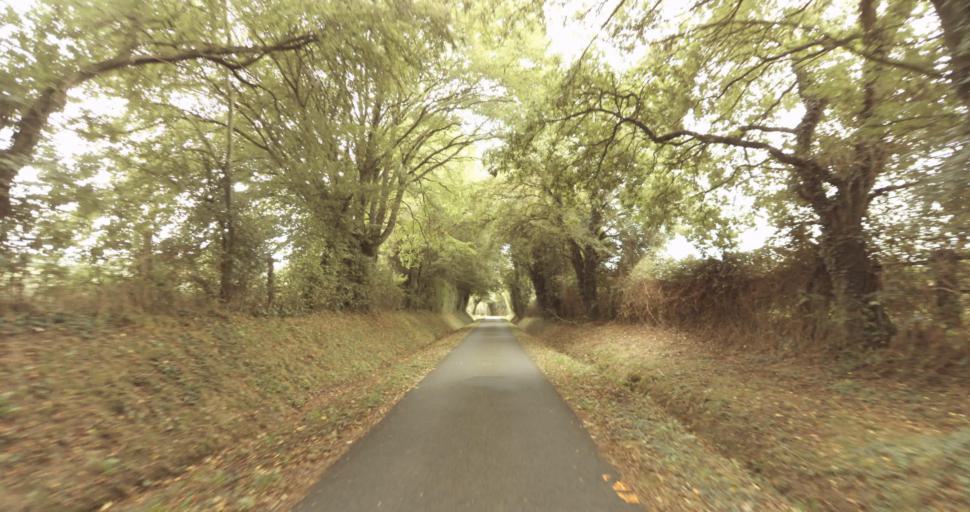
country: FR
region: Lower Normandy
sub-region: Departement de l'Orne
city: Gace
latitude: 48.6810
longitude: 0.3173
